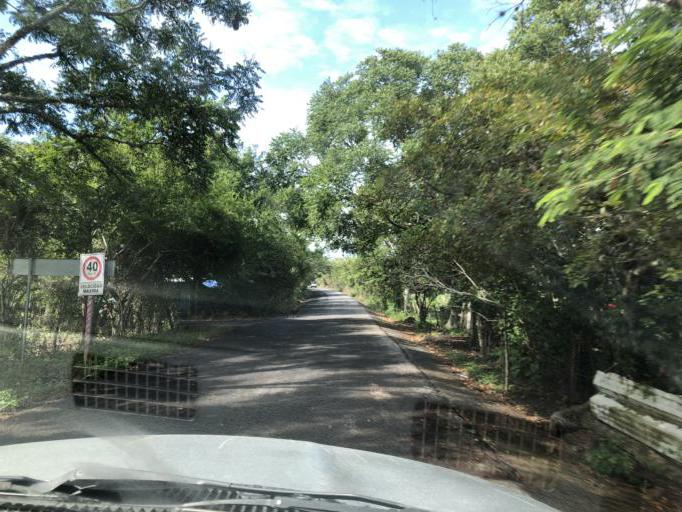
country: MX
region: Veracruz
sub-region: Alto Lucero de Gutierrez Barrios
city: Palma Sola
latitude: 19.8002
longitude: -96.5453
